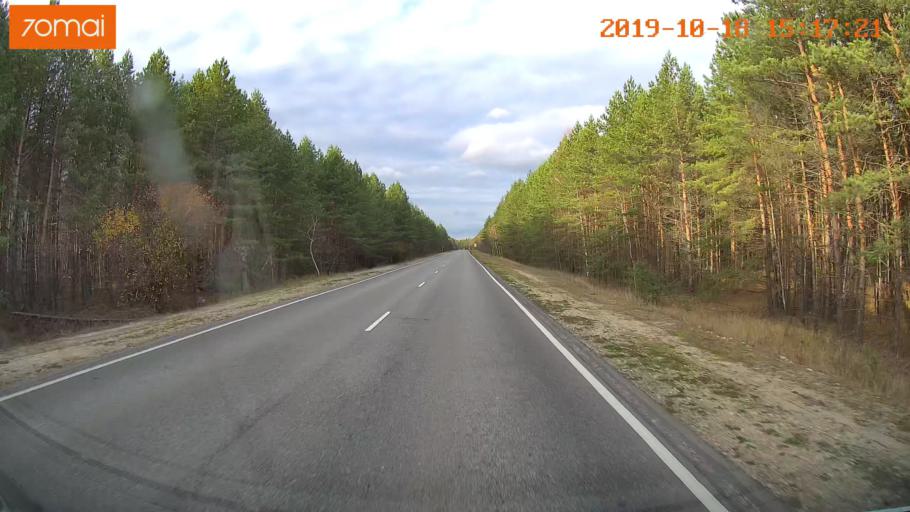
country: RU
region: Vladimir
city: Anopino
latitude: 55.6483
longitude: 40.7264
